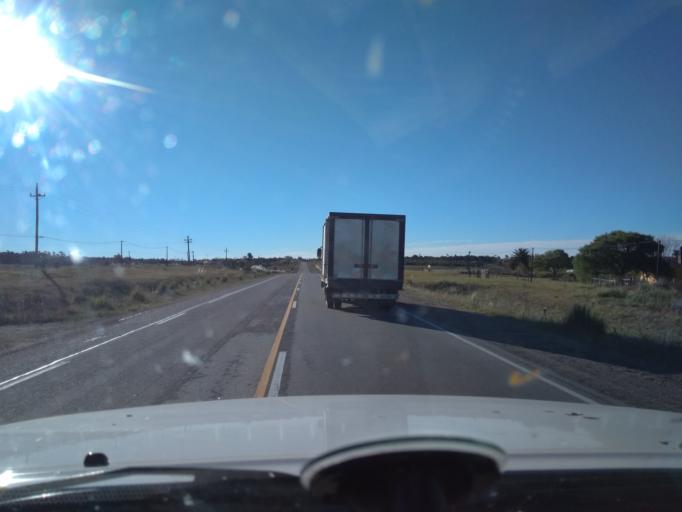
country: UY
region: Canelones
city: Sauce
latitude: -34.5889
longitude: -56.0537
